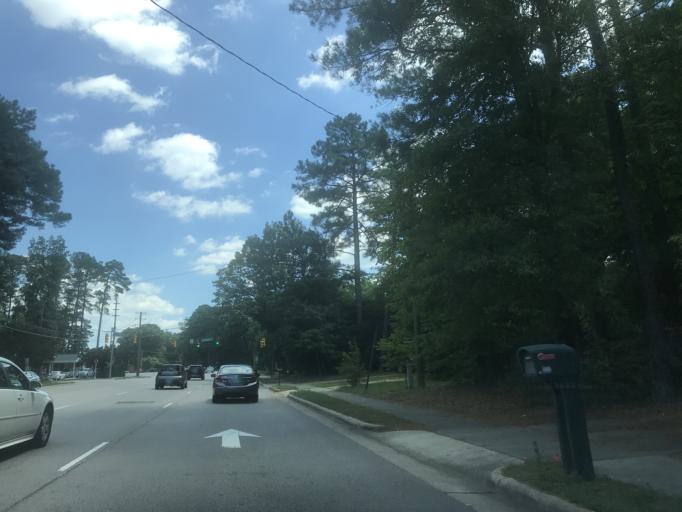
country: US
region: North Carolina
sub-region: Wake County
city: Cary
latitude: 35.7674
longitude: -78.7581
